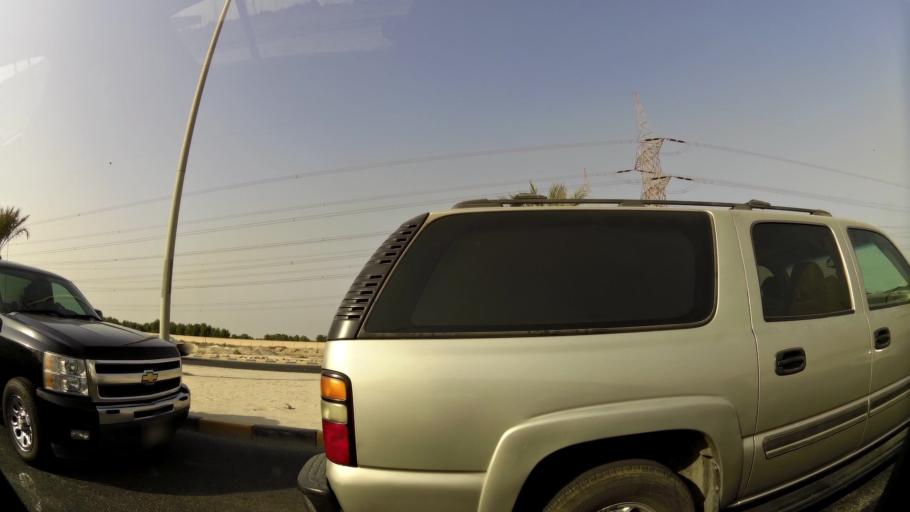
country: KW
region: Al Asimah
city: Ar Rabiyah
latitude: 29.2951
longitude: 47.8513
